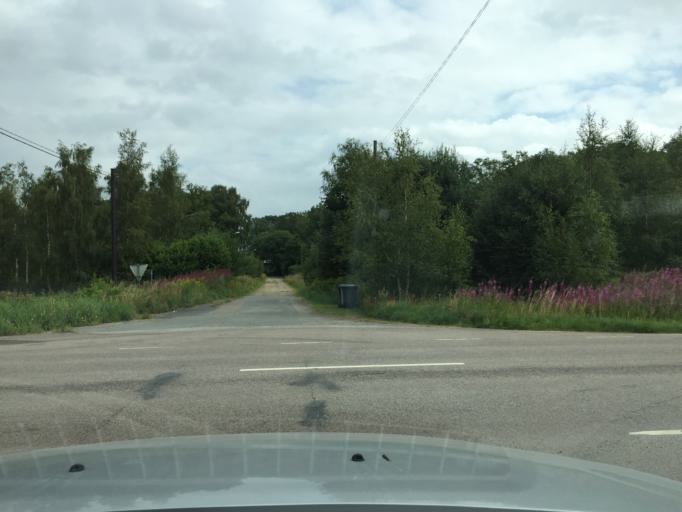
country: SE
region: Skane
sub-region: Hassleholms Kommun
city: Sosdala
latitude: 56.0294
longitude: 13.6859
